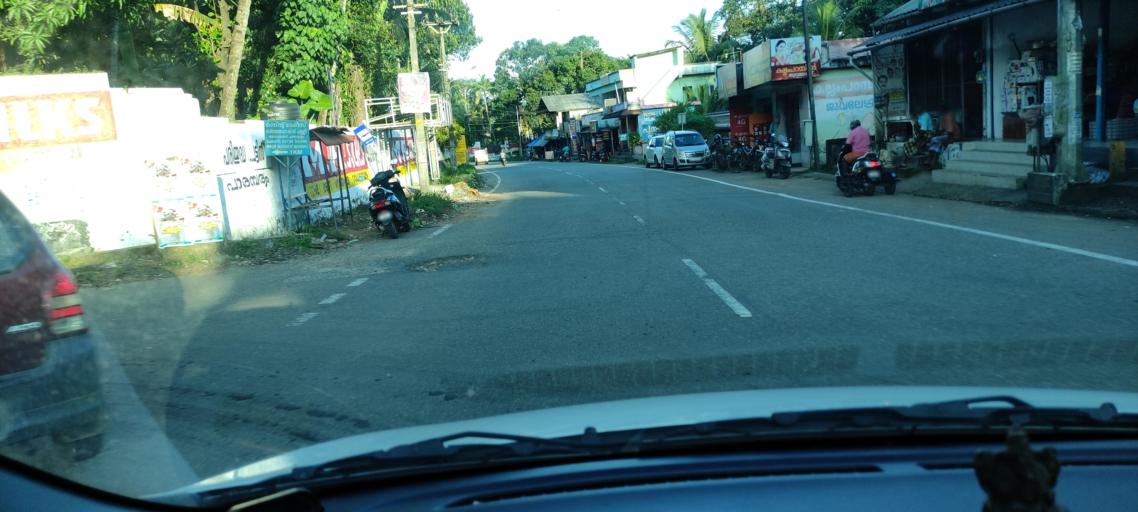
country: IN
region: Kerala
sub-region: Pattanamtitta
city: Adur
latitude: 9.1427
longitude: 76.7789
